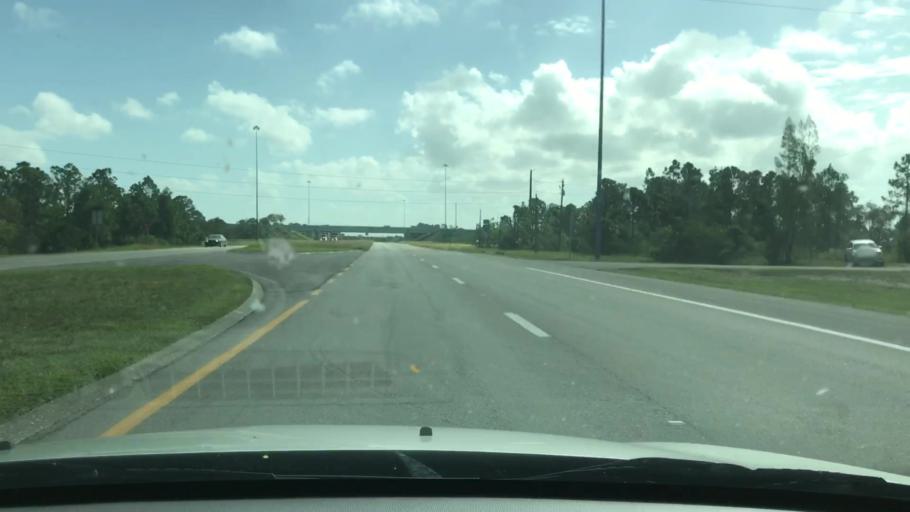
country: US
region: Florida
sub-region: Charlotte County
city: Charlotte Park
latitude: 26.8581
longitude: -81.9758
